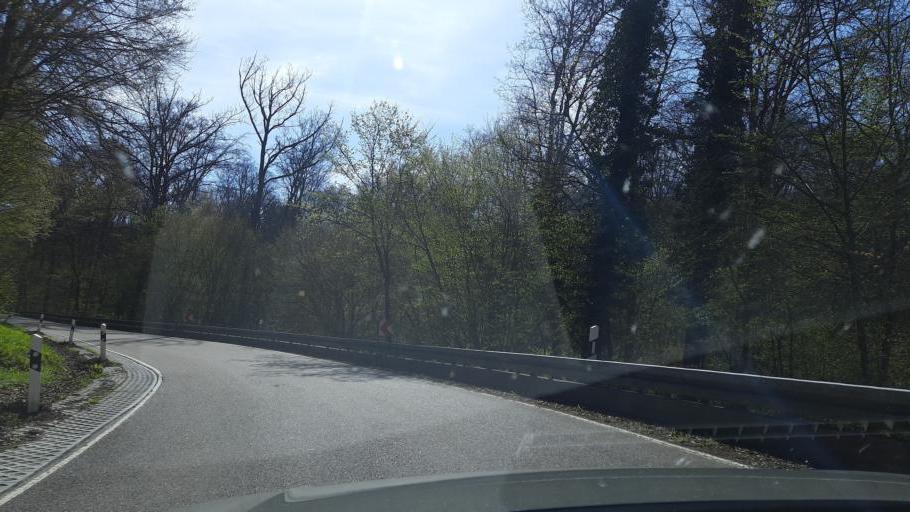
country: DE
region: Baden-Wuerttemberg
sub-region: Regierungsbezirk Stuttgart
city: Mockmuhl
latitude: 49.2756
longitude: 9.3751
